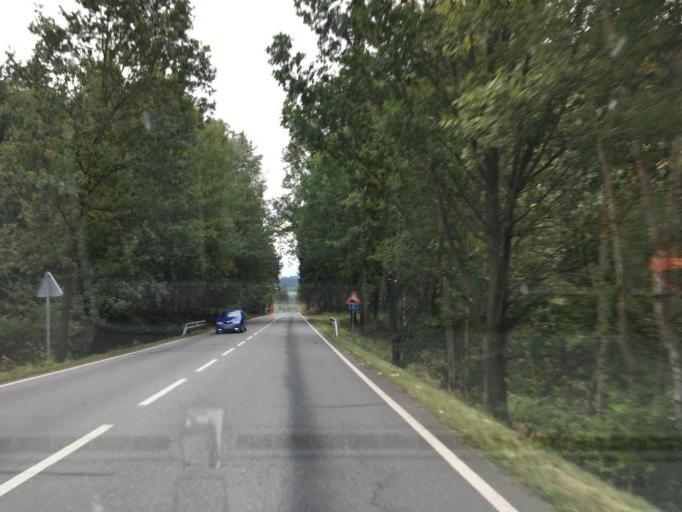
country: CZ
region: Vysocina
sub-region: Okres Pelhrimov
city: Zeliv
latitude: 49.4803
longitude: 15.1818
